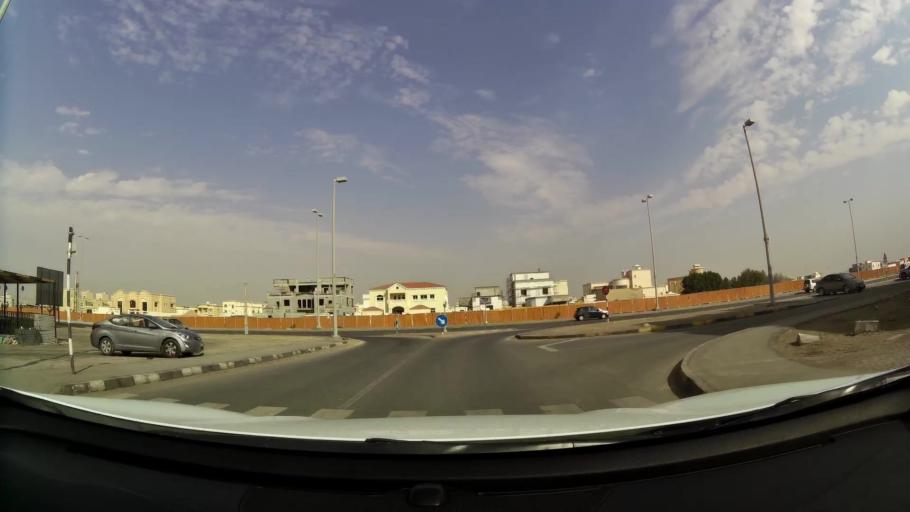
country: AE
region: Abu Dhabi
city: Abu Dhabi
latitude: 24.3269
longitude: 54.5385
